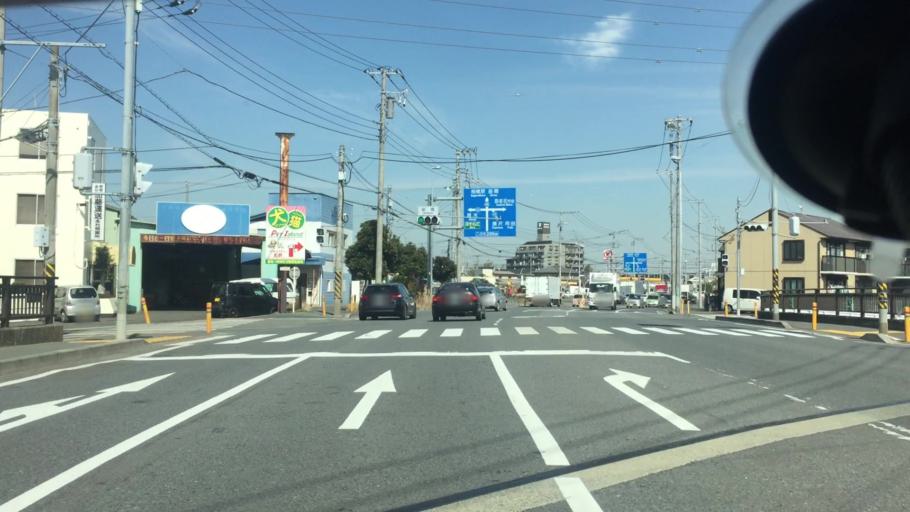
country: JP
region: Kanagawa
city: Atsugi
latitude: 35.4339
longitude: 139.3830
